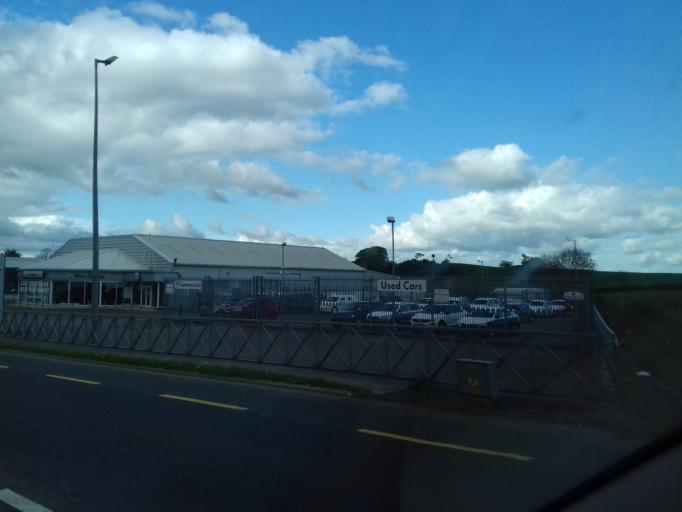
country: IE
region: Leinster
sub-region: Kilkenny
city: Kilkenny
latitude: 52.6276
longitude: -7.2511
